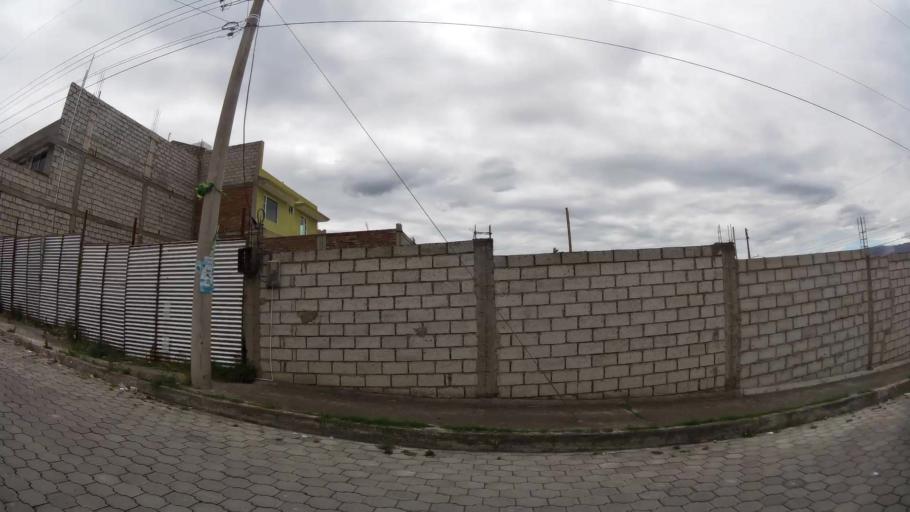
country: EC
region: Cotopaxi
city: Latacunga
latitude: -0.9521
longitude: -78.6042
